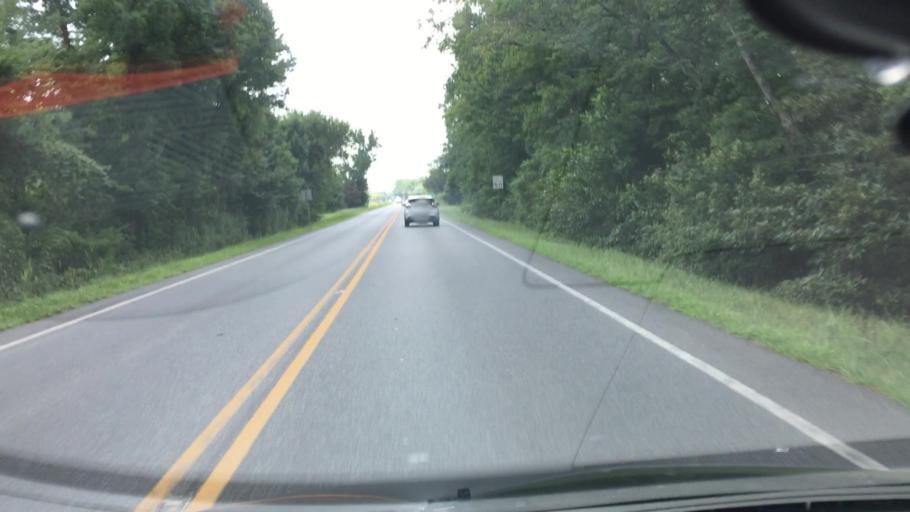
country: US
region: Maryland
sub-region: Worcester County
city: Ocean Pines
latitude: 38.3575
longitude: -75.1689
